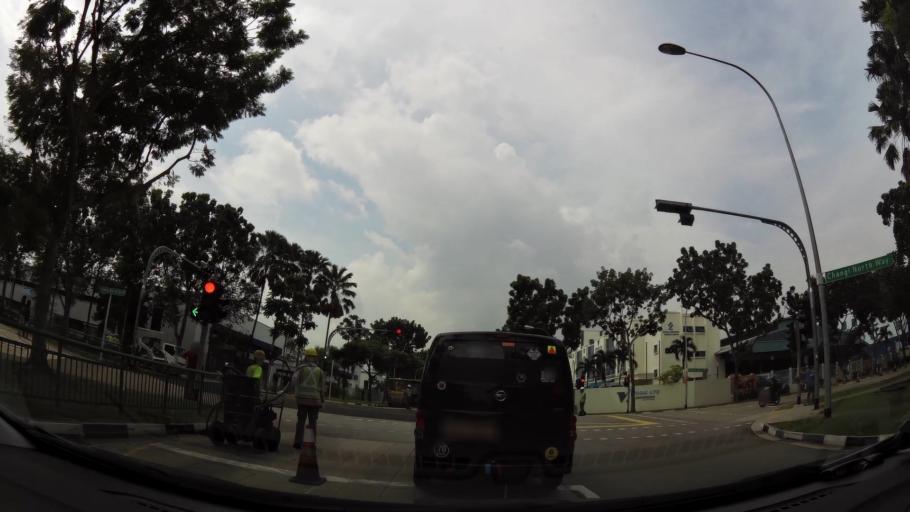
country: SG
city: Singapore
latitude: 1.3510
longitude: 103.9688
